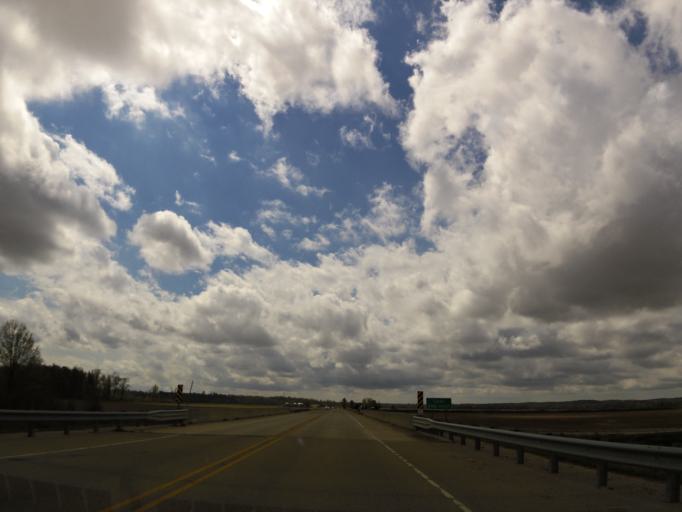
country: US
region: Arkansas
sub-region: Greene County
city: Marmaduke
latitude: 36.2487
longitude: -90.5351
